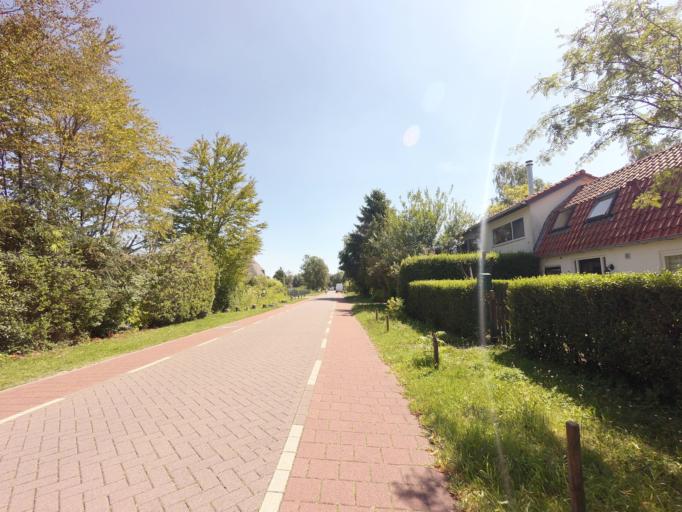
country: NL
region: Utrecht
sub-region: Stichtse Vecht
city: Maarssen
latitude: 52.1462
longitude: 5.0862
